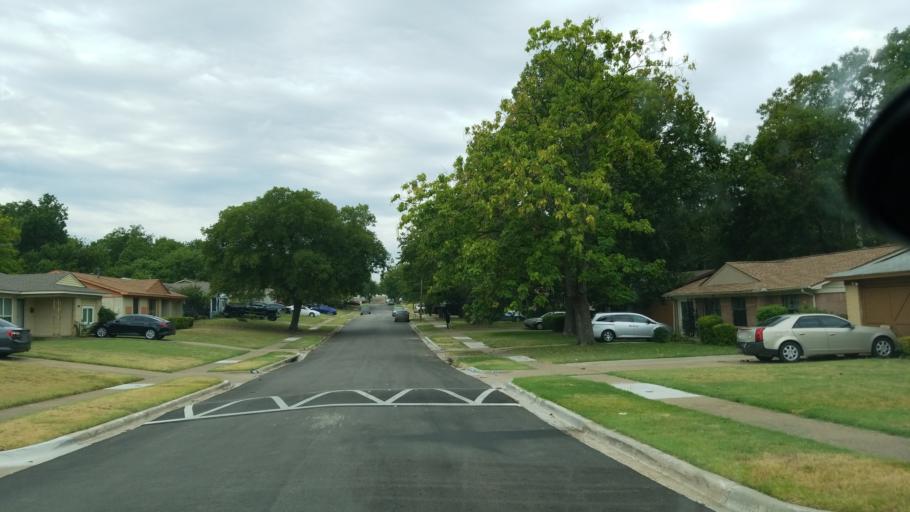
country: US
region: Texas
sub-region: Dallas County
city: Duncanville
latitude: 32.6607
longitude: -96.8366
